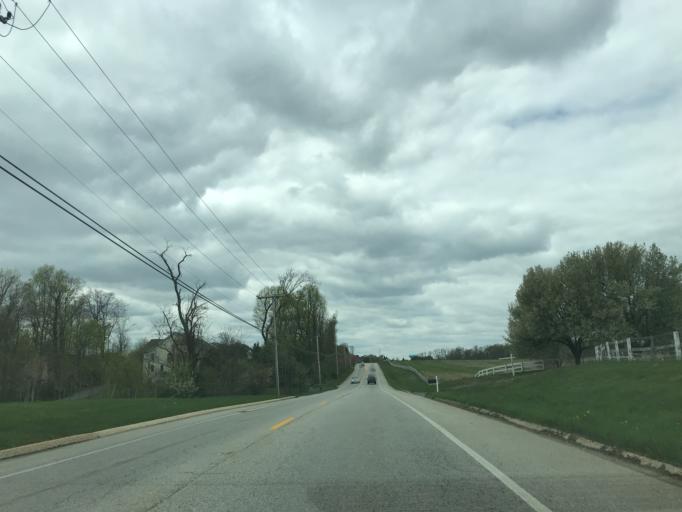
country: US
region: Maryland
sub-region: Harford County
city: Bel Air South
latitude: 39.5261
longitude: -76.2887
